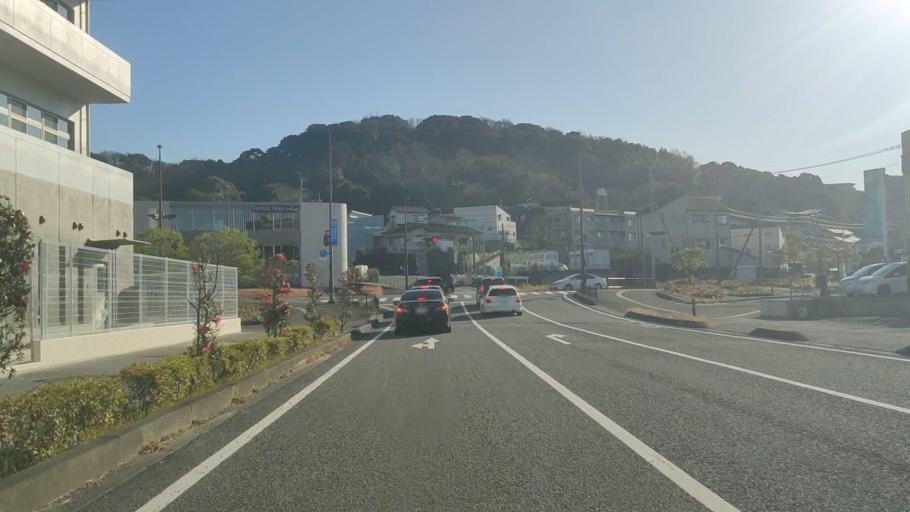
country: JP
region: Oita
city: Oita
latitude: 33.2281
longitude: 131.6014
